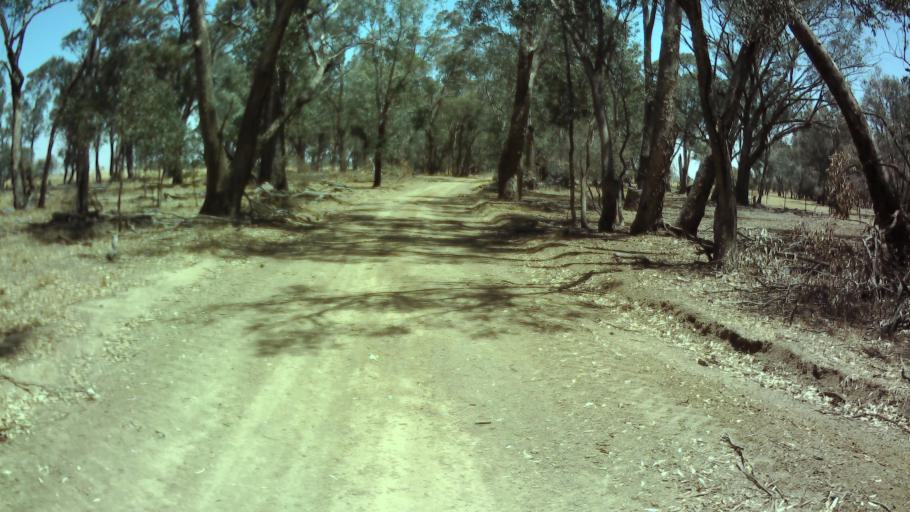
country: AU
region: New South Wales
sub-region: Weddin
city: Grenfell
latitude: -34.0466
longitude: 147.8354
